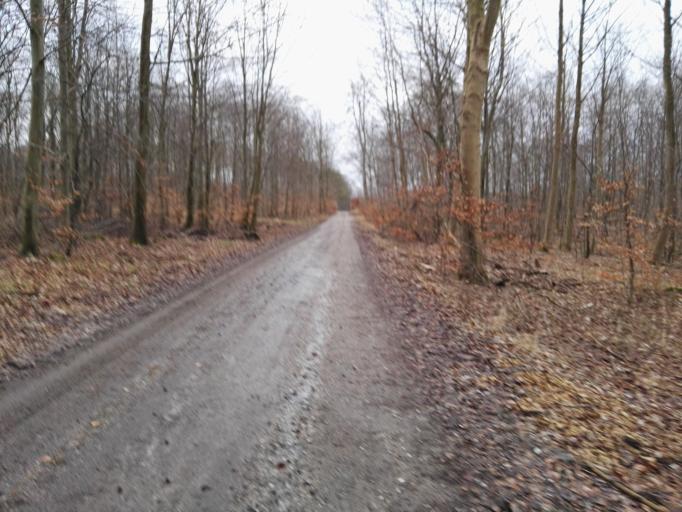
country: DK
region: Zealand
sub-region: Lejre Kommune
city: Lejre
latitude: 55.6433
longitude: 11.9303
